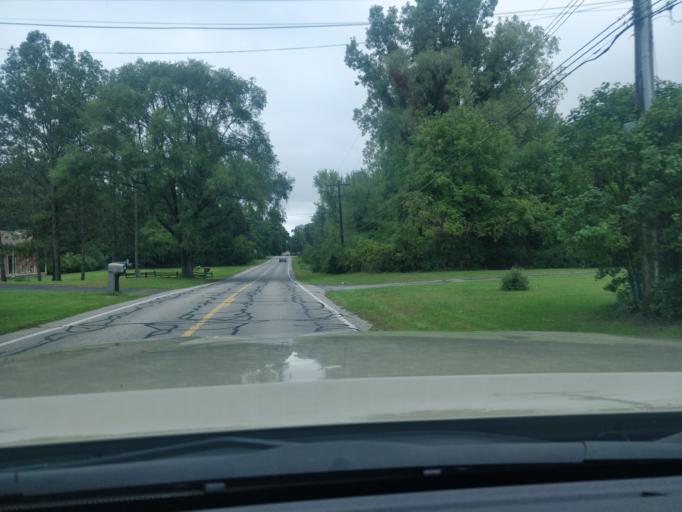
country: US
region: Michigan
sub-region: Wayne County
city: Romulus
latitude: 42.1969
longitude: -83.4237
